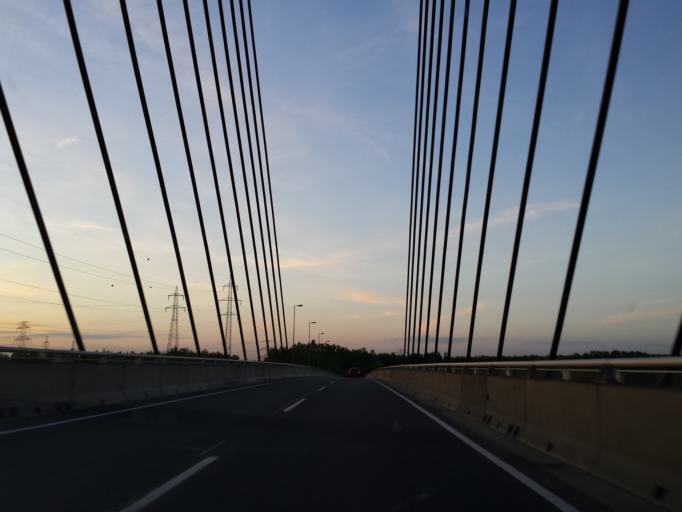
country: AT
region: Lower Austria
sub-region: Politischer Bezirk Tulln
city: Tulln
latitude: 48.3344
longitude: 16.0277
